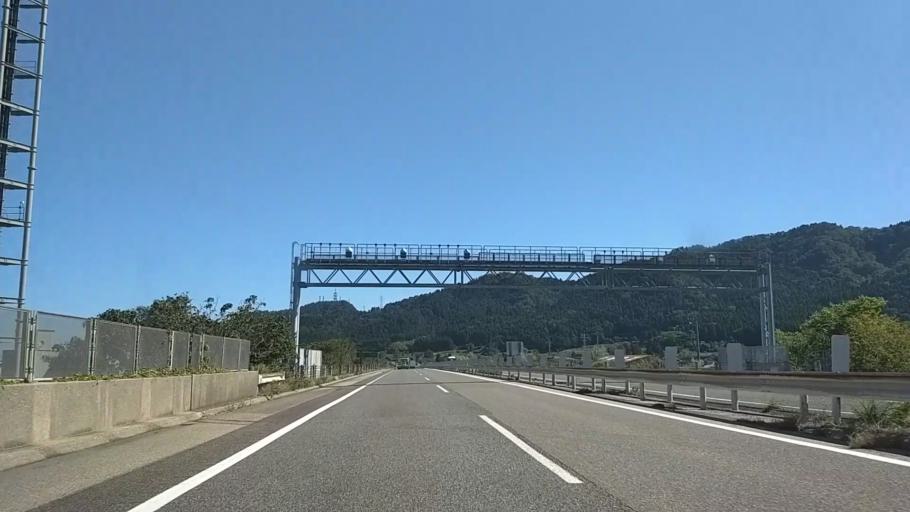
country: JP
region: Toyama
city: Nyuzen
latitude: 36.9458
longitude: 137.5611
